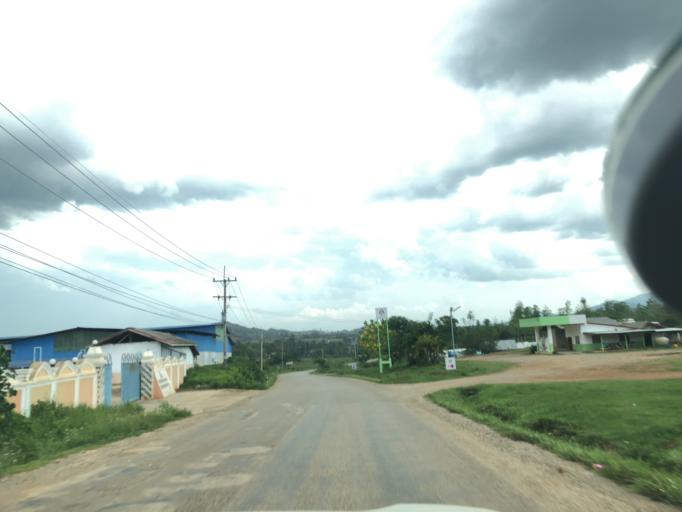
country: TH
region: Uttaradit
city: Ban Khok
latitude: 18.1186
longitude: 101.3728
